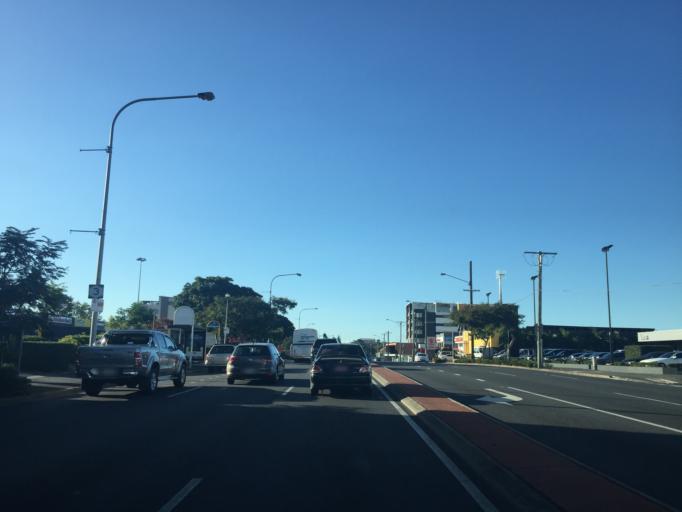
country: AU
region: Queensland
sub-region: Brisbane
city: Windsor
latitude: -27.4377
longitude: 153.0310
